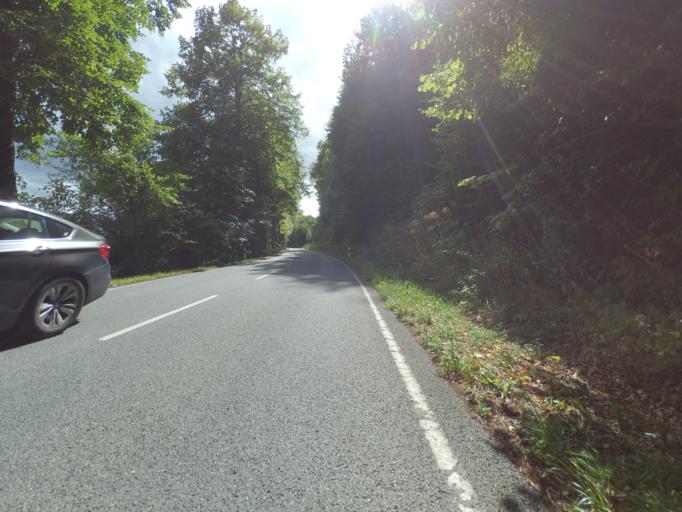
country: LU
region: Grevenmacher
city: Gonderange
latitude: 49.6624
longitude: 6.2280
